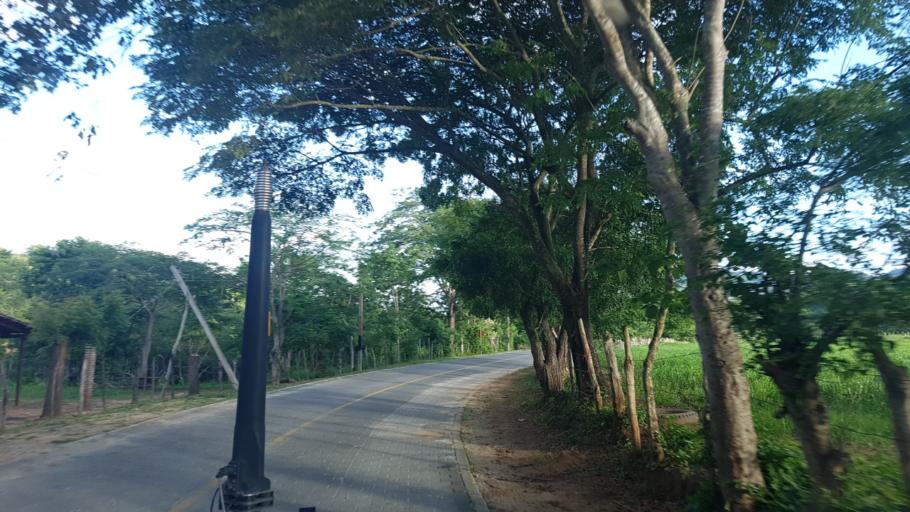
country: NI
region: Nueva Segovia
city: Ocotal
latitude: 13.6443
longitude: -86.5944
